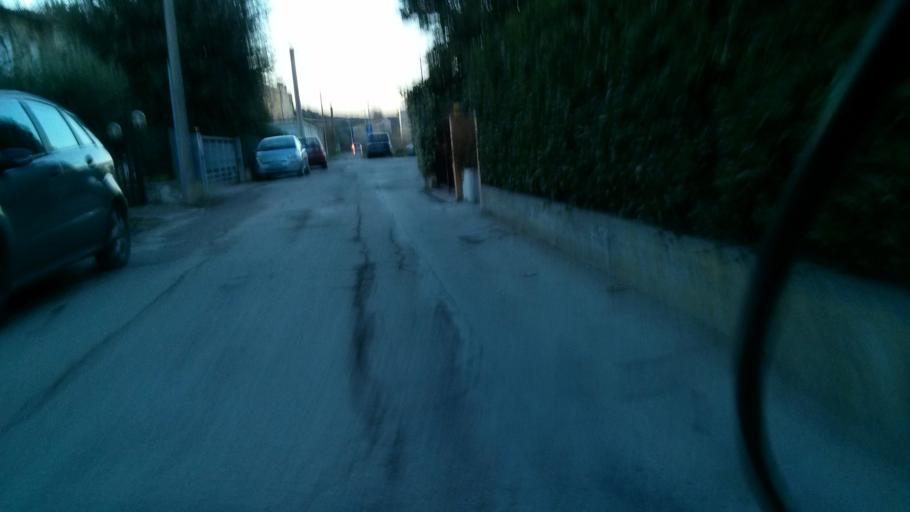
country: IT
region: The Marches
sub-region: Provincia di Pesaro e Urbino
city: Fano
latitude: 43.8479
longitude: 13.0036
